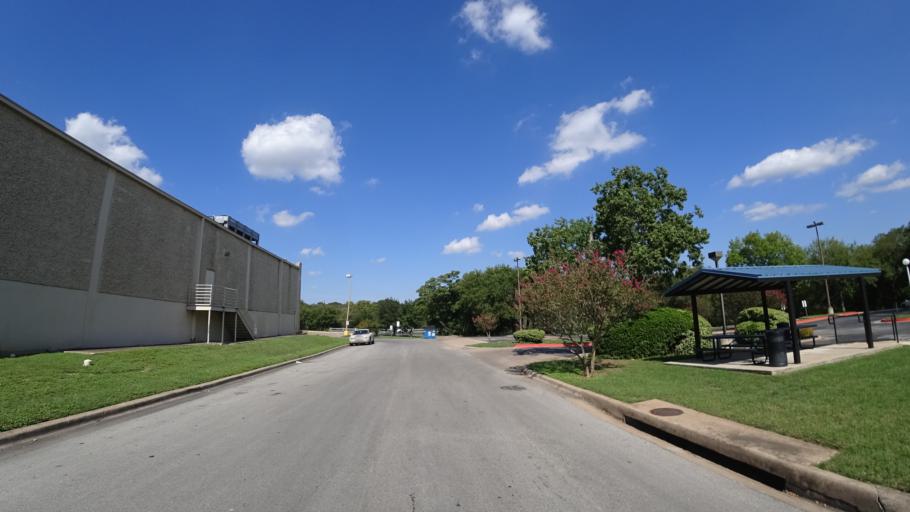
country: US
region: Texas
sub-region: Travis County
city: Austin
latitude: 30.3065
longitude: -97.7487
